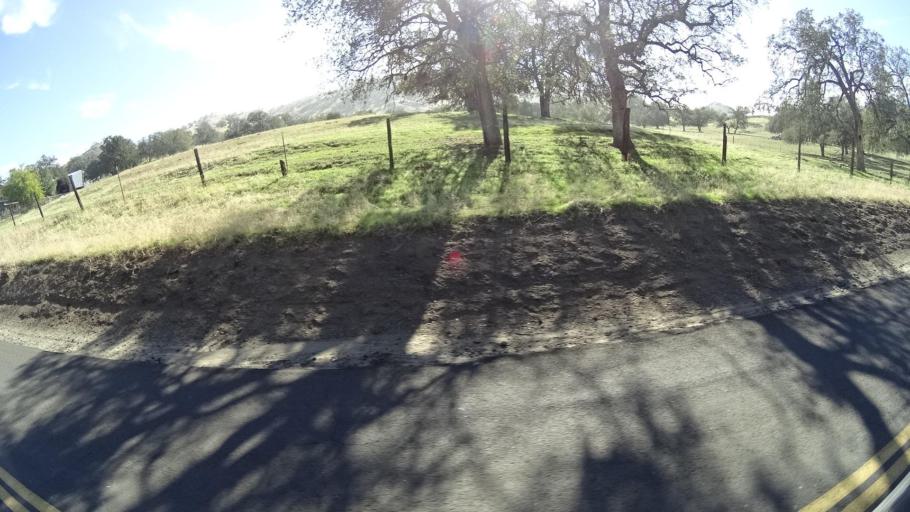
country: US
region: California
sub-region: Tulare County
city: Richgrove
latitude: 35.6994
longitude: -118.8505
